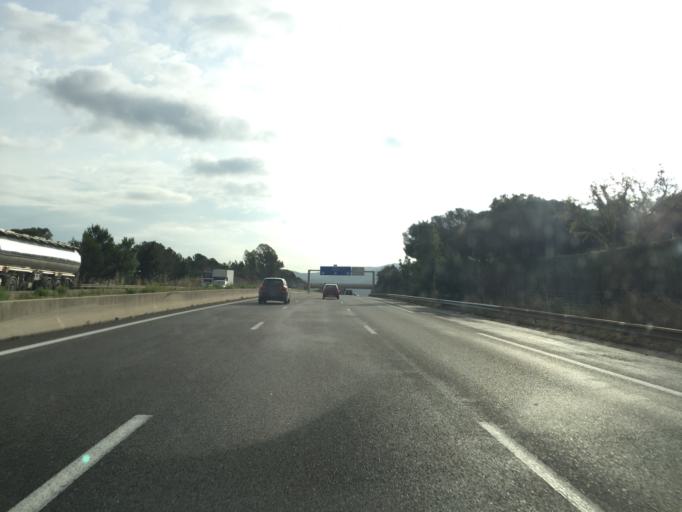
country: FR
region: Provence-Alpes-Cote d'Azur
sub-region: Departement du Var
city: Frejus
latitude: 43.4655
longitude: 6.7198
